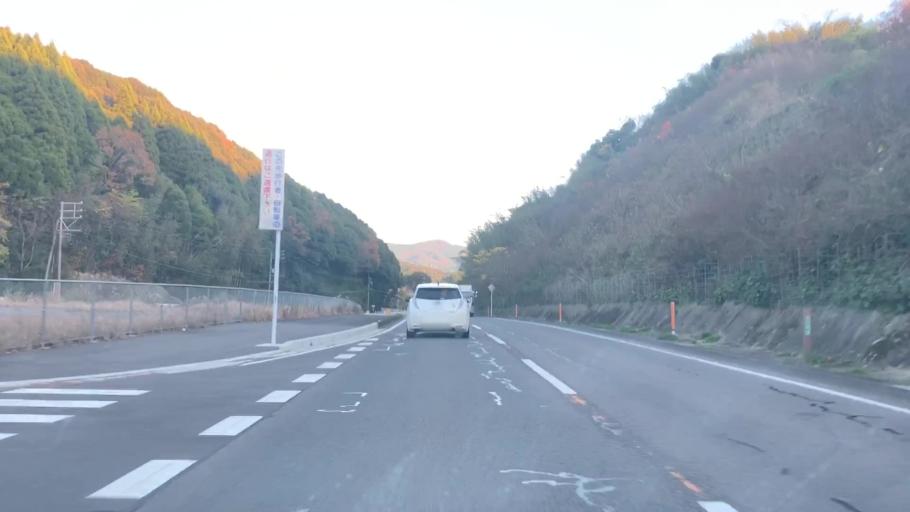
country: JP
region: Saga Prefecture
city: Takeocho-takeo
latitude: 33.2631
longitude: 129.9691
